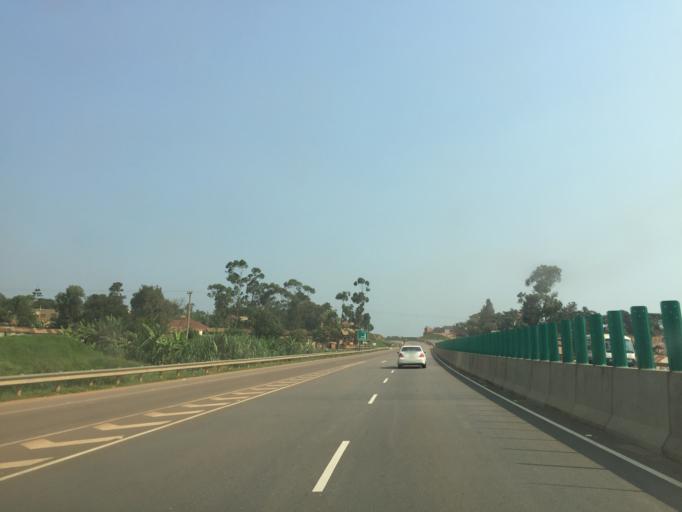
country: UG
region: Central Region
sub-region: Wakiso District
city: Kajansi
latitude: 0.2107
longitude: 32.5442
